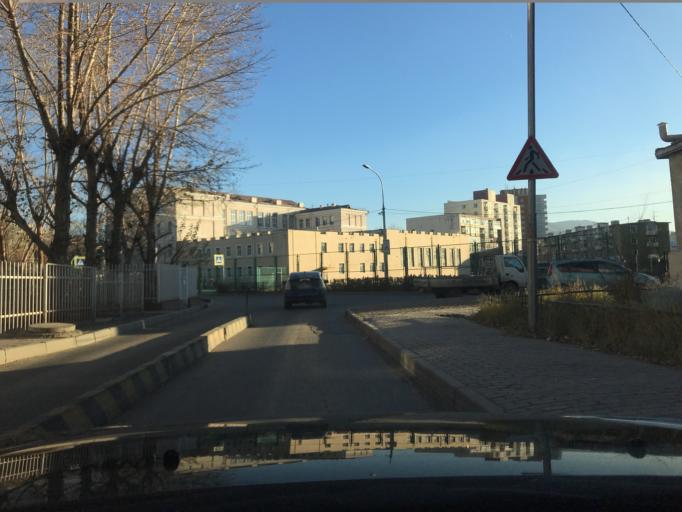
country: MN
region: Ulaanbaatar
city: Ulaanbaatar
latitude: 47.9262
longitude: 106.9109
